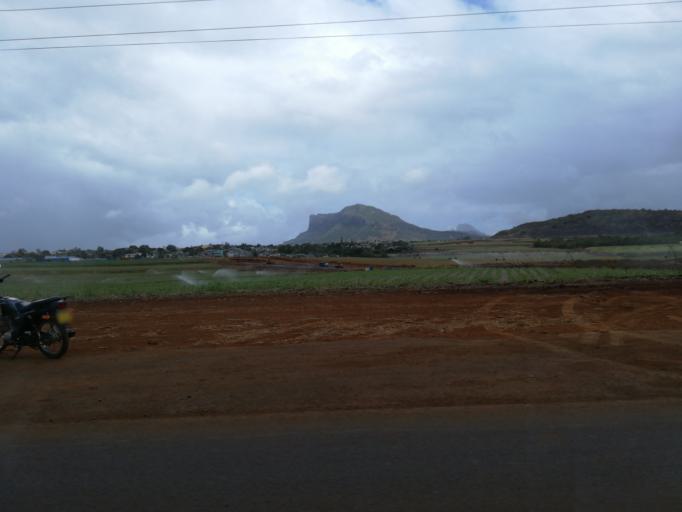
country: MU
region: Black River
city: Petite Riviere
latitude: -20.2146
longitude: 57.4560
